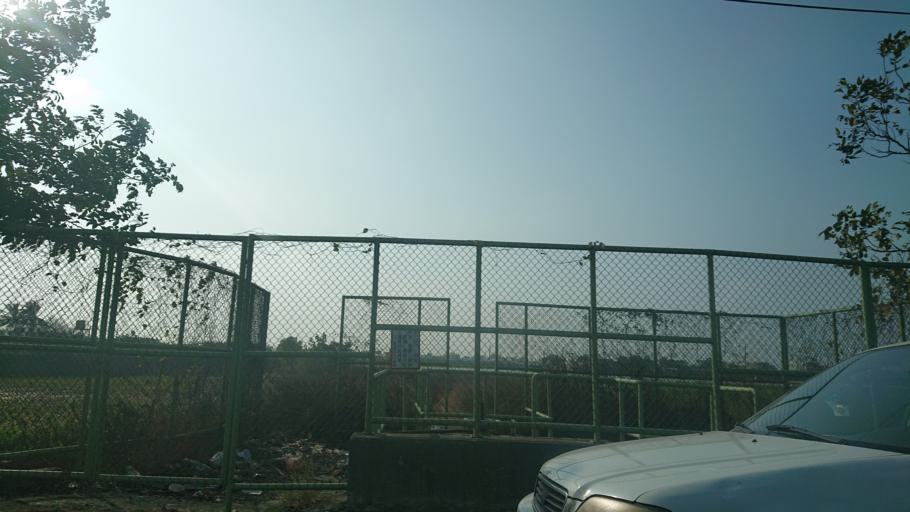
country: TW
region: Taiwan
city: Xinying
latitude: 23.2062
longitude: 120.2719
